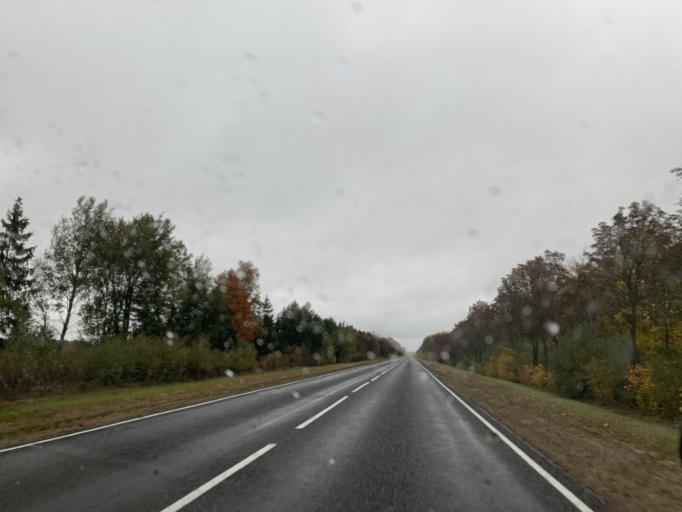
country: BY
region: Minsk
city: Haradzyeya
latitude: 53.3931
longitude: 26.5803
